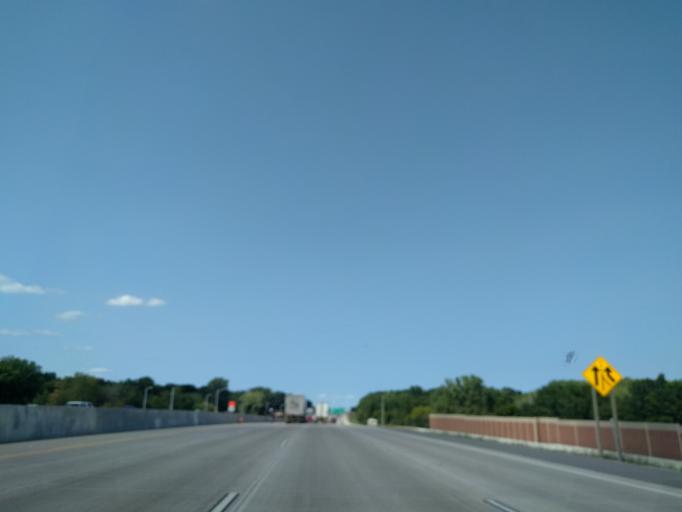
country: US
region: Wisconsin
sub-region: Brown County
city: Ashwaubenon
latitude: 44.5101
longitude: -88.0825
